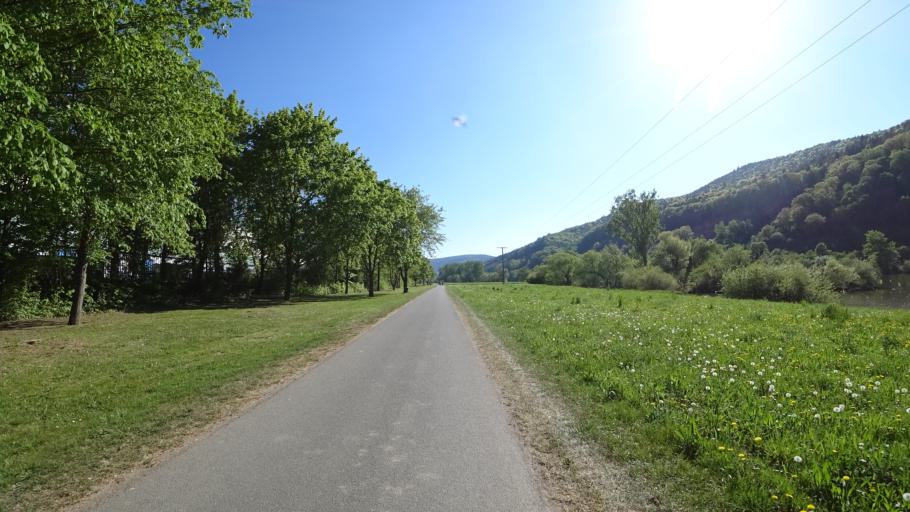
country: DE
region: Bavaria
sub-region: Regierungsbezirk Unterfranken
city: Burgstadt
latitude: 49.7309
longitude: 9.2712
